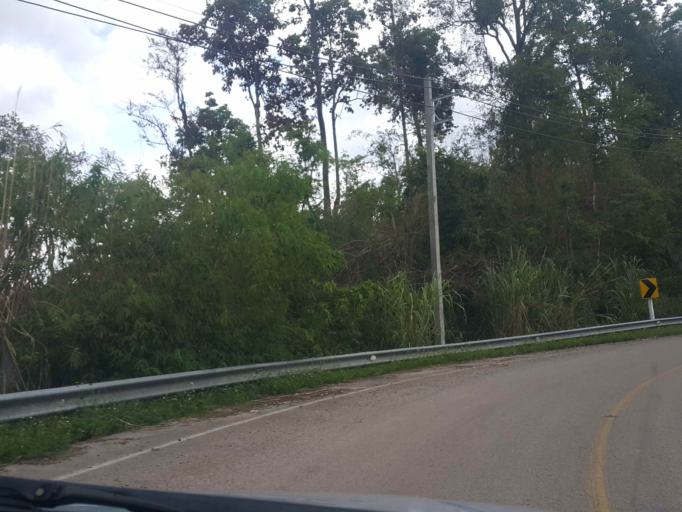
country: TH
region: Lampang
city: Ngao
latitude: 18.9338
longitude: 100.0892
